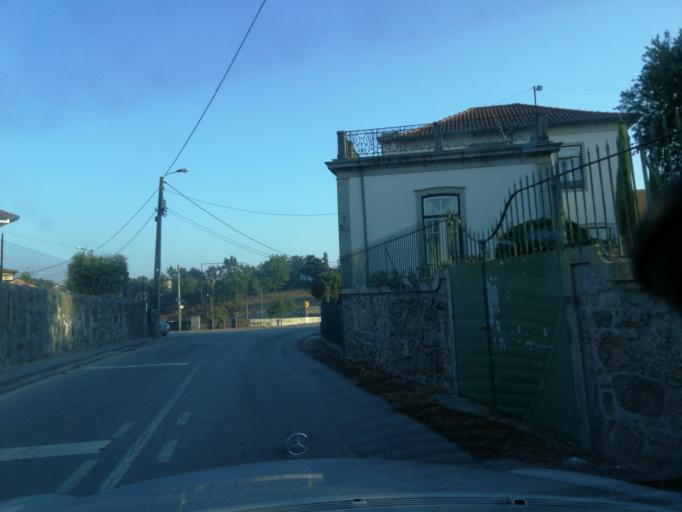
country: PT
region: Braga
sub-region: Braga
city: Braga
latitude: 41.5193
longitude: -8.4343
